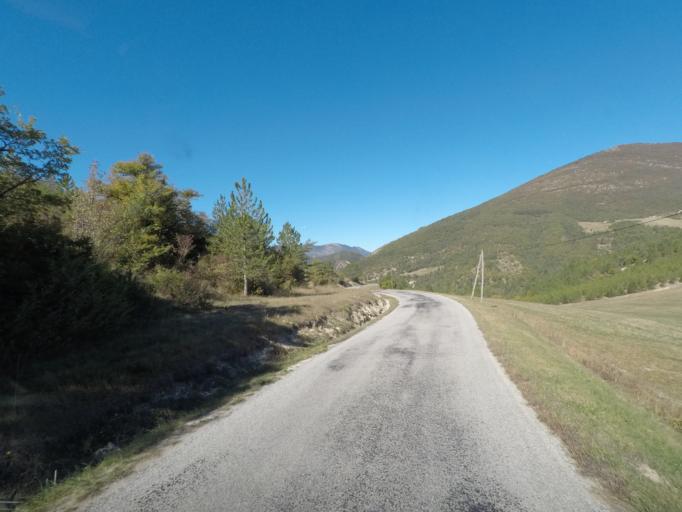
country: FR
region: Rhone-Alpes
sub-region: Departement de la Drome
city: Die
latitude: 44.5606
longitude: 5.3381
